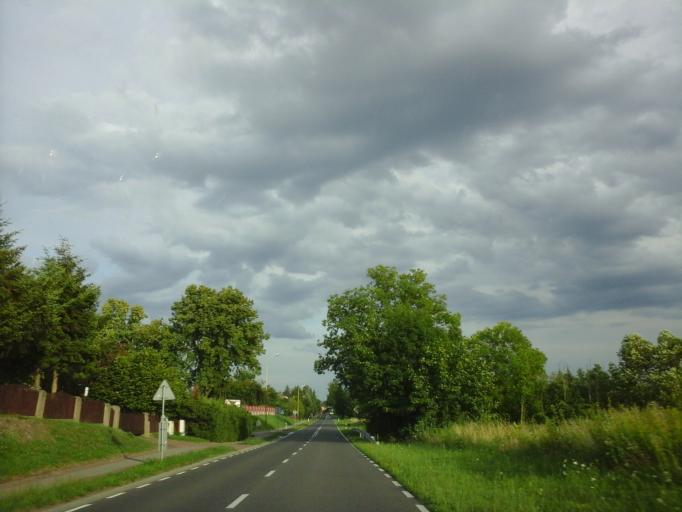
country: PL
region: West Pomeranian Voivodeship
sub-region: Powiat kamienski
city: Golczewo
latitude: 53.8286
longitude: 14.9701
